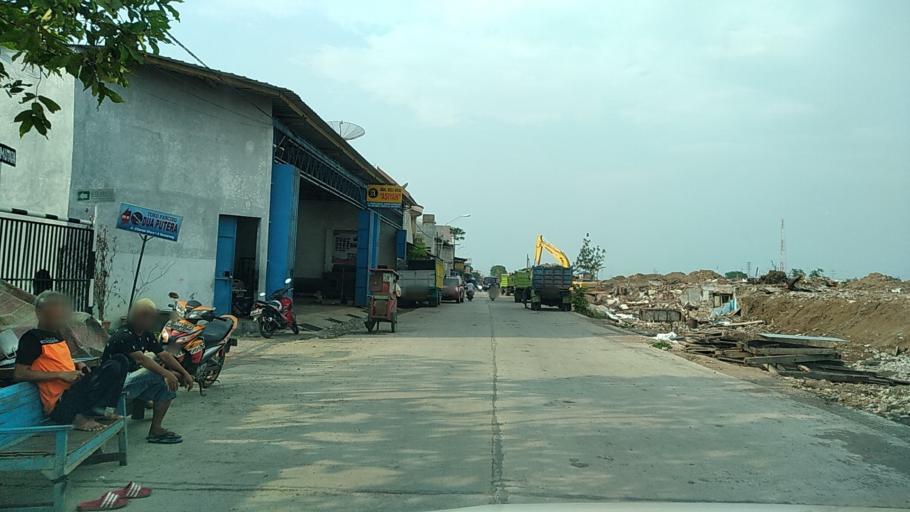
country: ID
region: Central Java
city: Semarang
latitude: -6.9701
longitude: 110.4425
